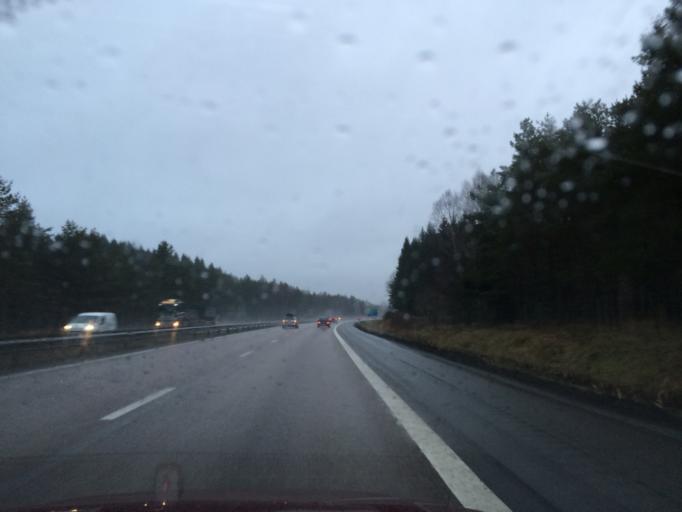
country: SE
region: Vaestra Goetaland
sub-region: Molndal
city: Lindome
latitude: 57.5623
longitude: 12.0531
